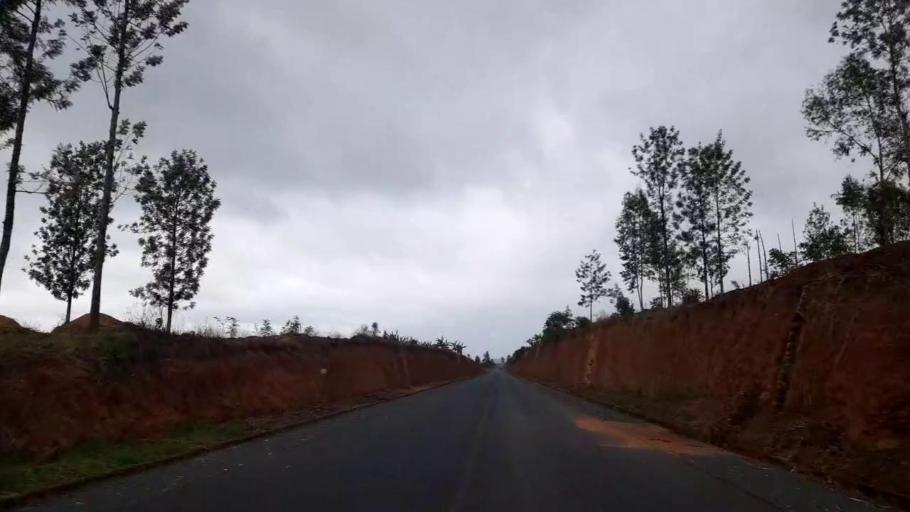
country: RW
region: Northern Province
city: Byumba
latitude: -1.4319
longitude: 30.2622
